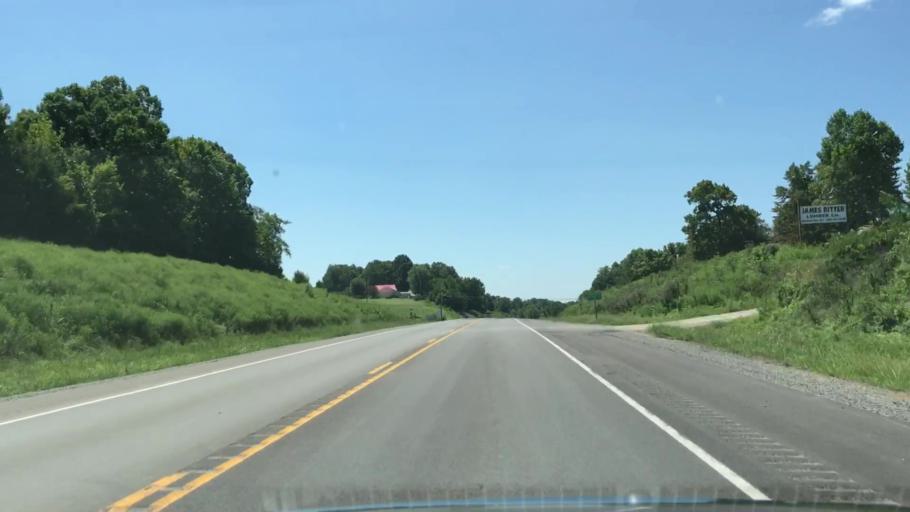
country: US
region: Kentucky
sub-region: Cumberland County
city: Burkesville
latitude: 36.6580
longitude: -85.3722
